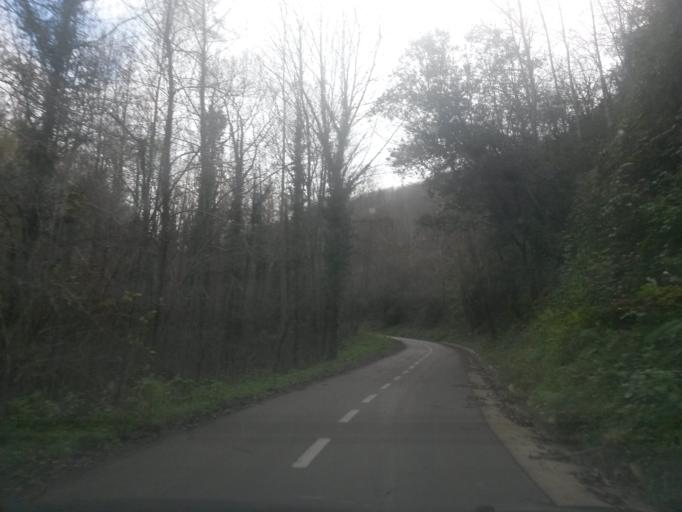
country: ES
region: Catalonia
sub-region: Provincia de Girona
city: Susqueda
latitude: 41.9676
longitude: 2.5273
